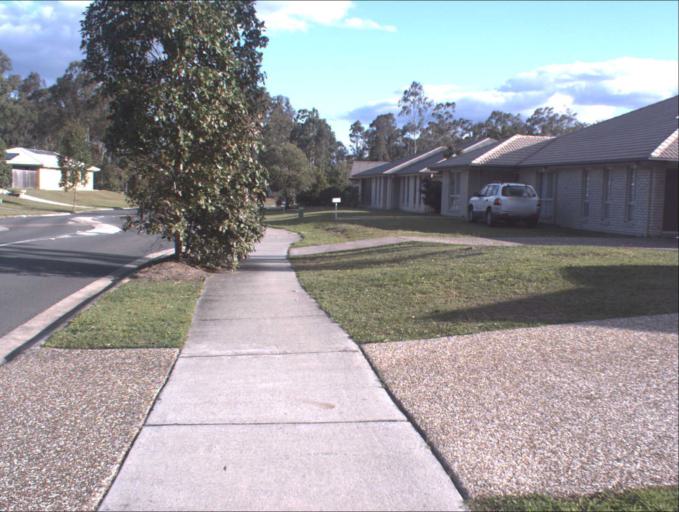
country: AU
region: Queensland
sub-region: Logan
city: North Maclean
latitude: -27.8048
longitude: 152.9529
